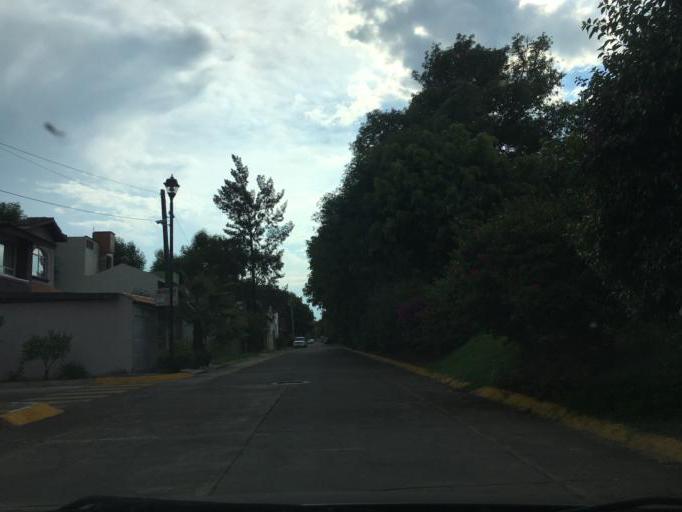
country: MX
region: Michoacan
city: Morelia
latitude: 19.6831
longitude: -101.2078
